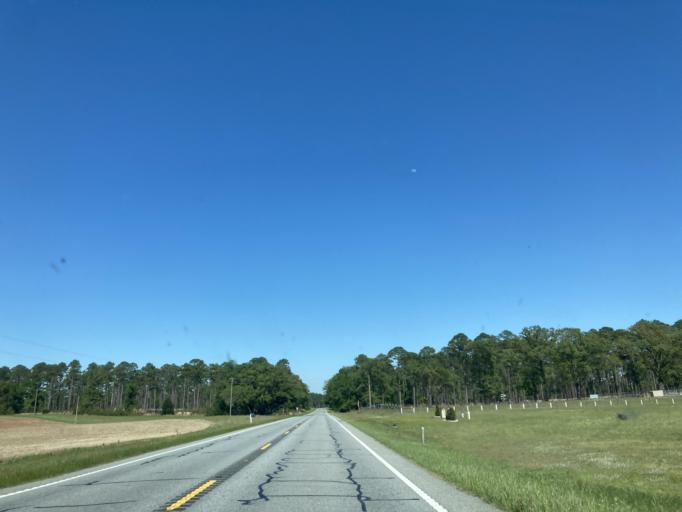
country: US
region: Georgia
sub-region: Baker County
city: Newton
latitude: 31.2098
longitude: -84.4876
